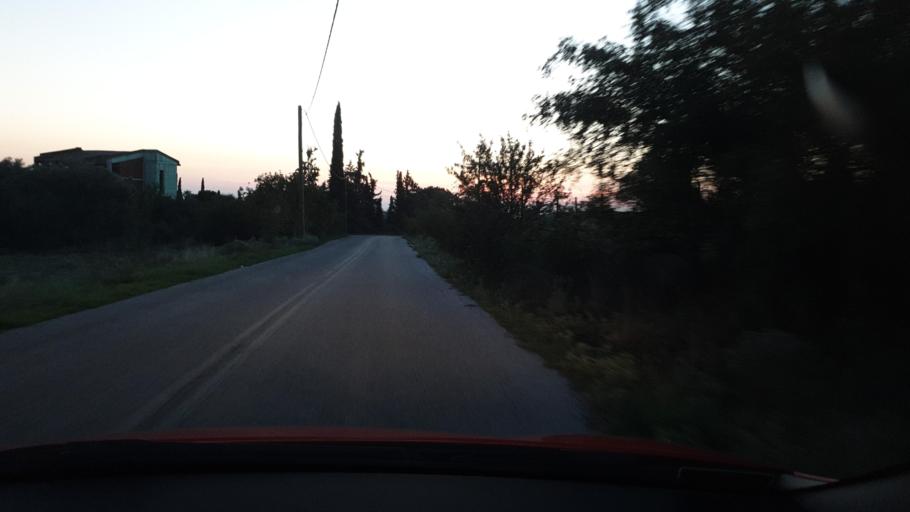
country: GR
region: Central Macedonia
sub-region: Nomos Thessalonikis
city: Vasilika
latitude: 40.5091
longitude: 23.1378
